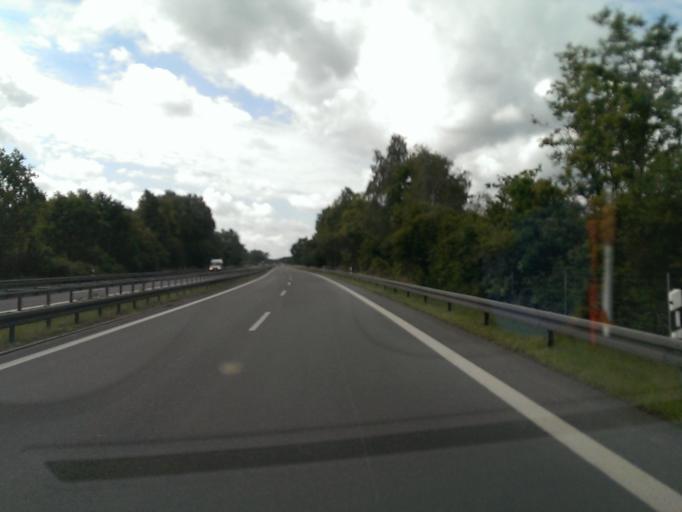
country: DE
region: Brandenburg
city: Calau
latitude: 51.7695
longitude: 13.8664
